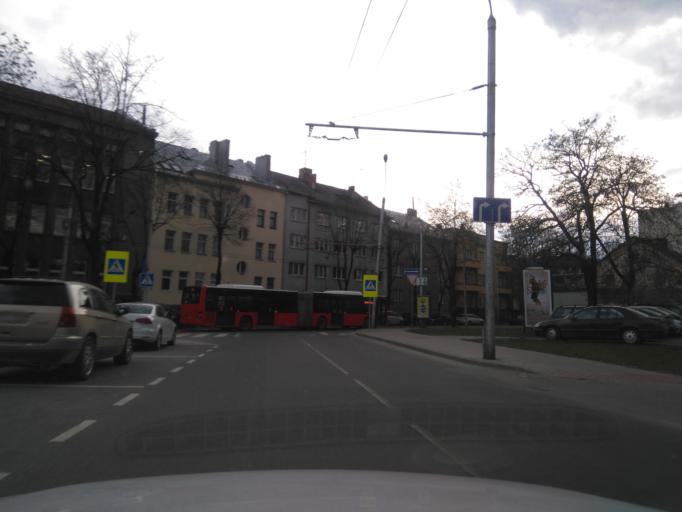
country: LT
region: Kauno apskritis
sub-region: Kaunas
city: Kaunas
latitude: 54.8956
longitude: 23.9247
